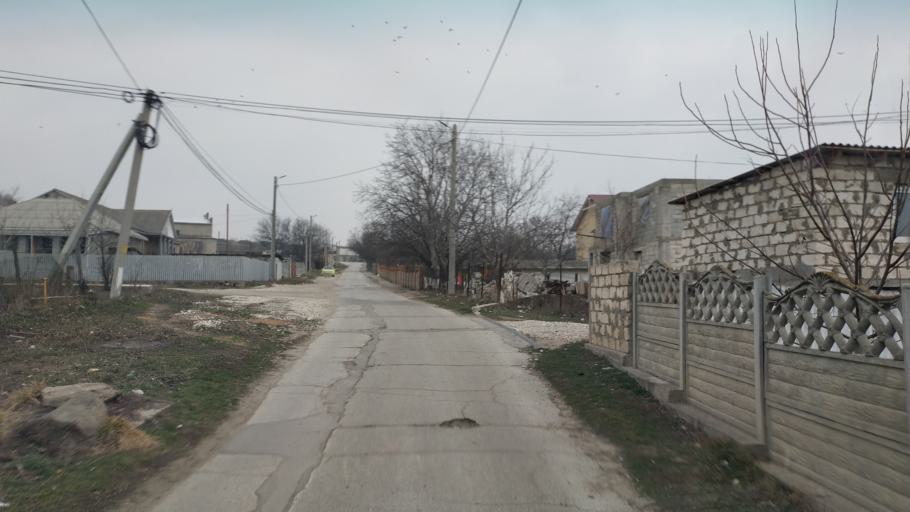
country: MD
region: Chisinau
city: Singera
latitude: 46.8203
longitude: 28.9696
